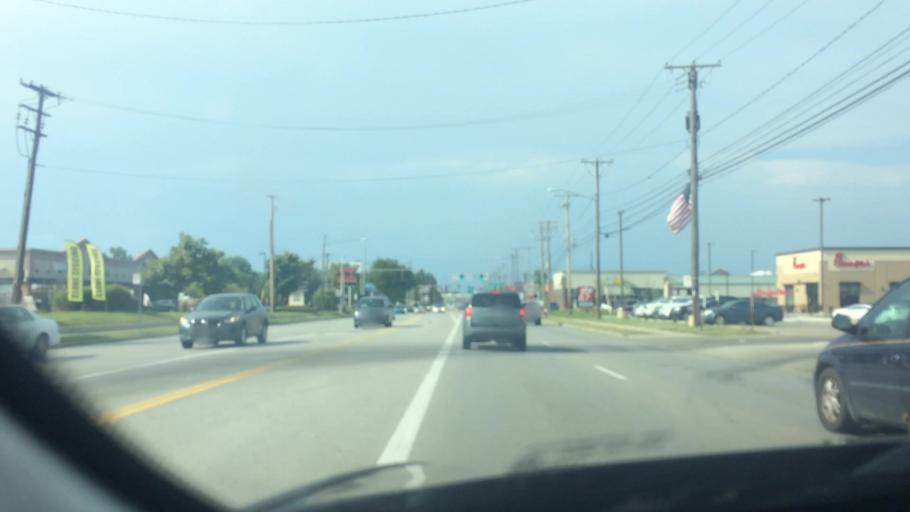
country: US
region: Ohio
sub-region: Lucas County
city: Ottawa Hills
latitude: 41.6801
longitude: -83.6227
